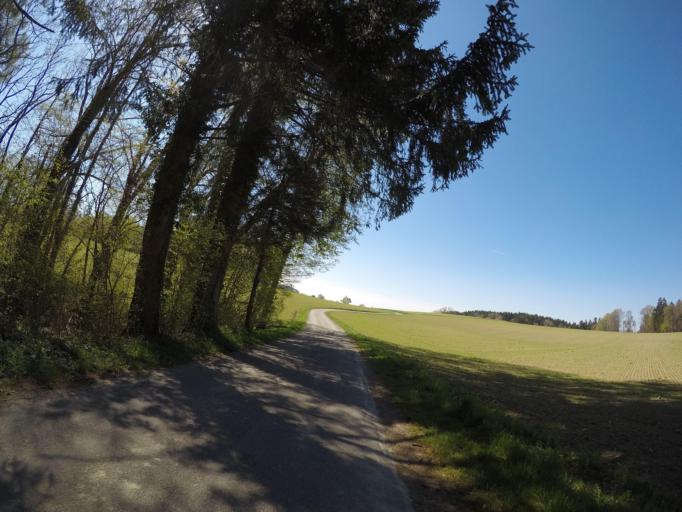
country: DE
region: Baden-Wuerttemberg
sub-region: Tuebingen Region
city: Markdorf
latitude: 47.7598
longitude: 9.3993
